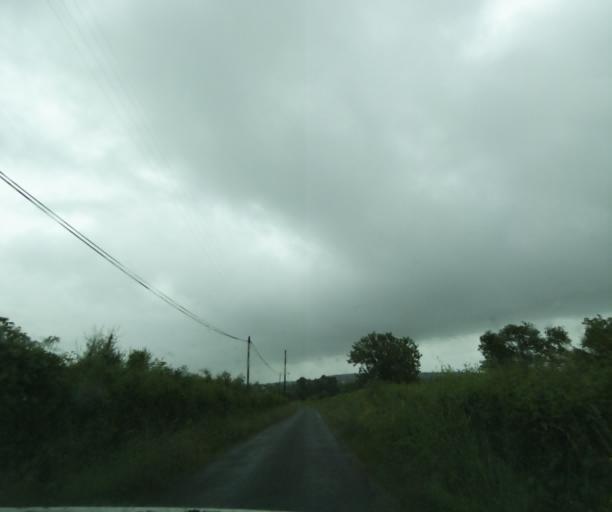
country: FR
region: Bourgogne
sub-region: Departement de Saone-et-Loire
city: Palinges
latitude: 46.5290
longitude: 4.2745
